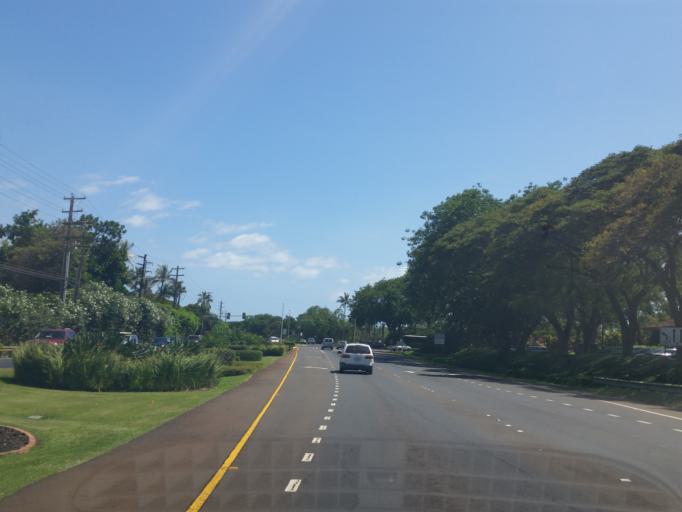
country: US
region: Hawaii
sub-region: Maui County
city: Ka'anapali
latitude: 20.9190
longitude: -156.6902
